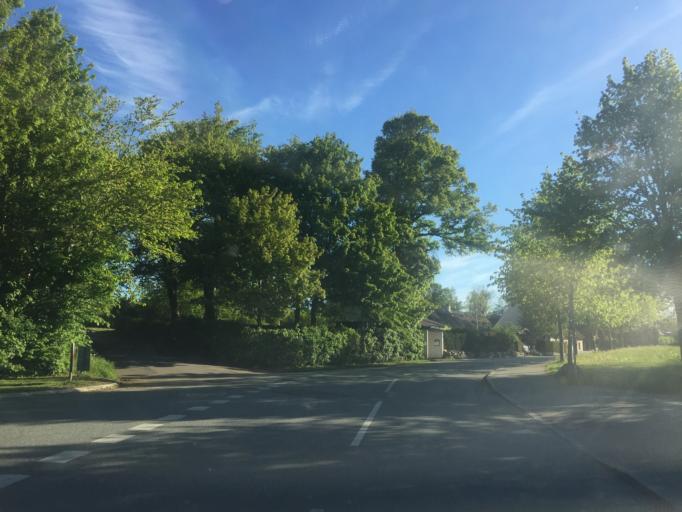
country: DK
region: Capital Region
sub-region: Egedal Kommune
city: Smorumnedre
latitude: 55.7343
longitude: 12.2682
